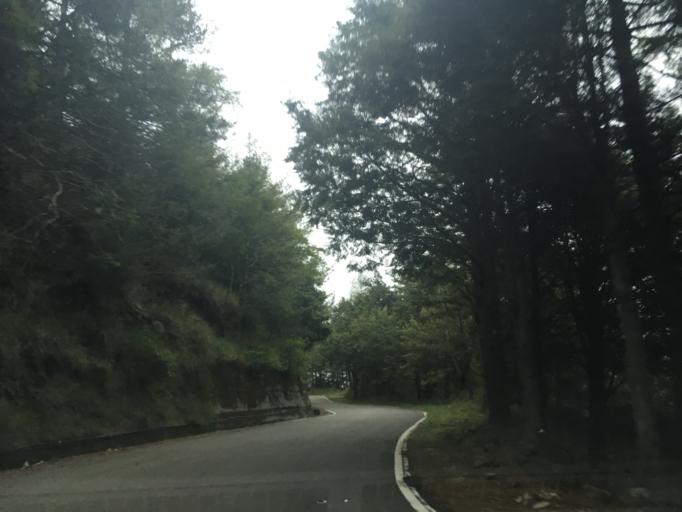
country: TW
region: Taiwan
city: Fengyuan
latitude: 24.2770
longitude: 121.0278
